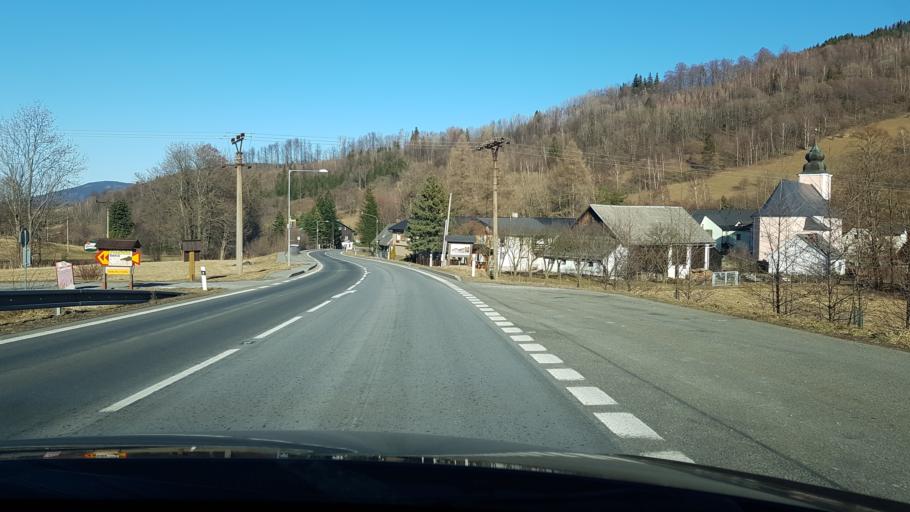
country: CZ
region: Olomoucky
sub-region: Okres Jesenik
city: Jesenik
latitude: 50.1602
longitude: 17.1933
